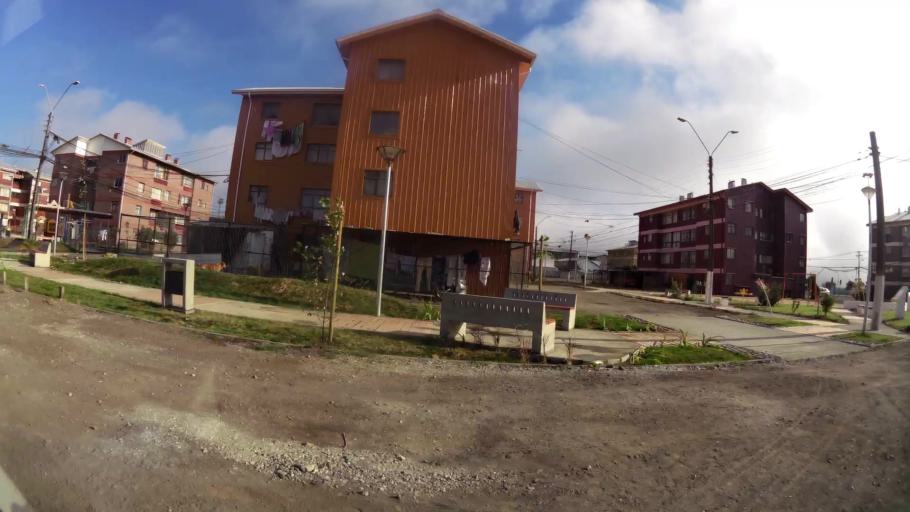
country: CL
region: Biobio
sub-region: Provincia de Concepcion
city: Concepcion
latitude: -36.7903
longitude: -73.0933
